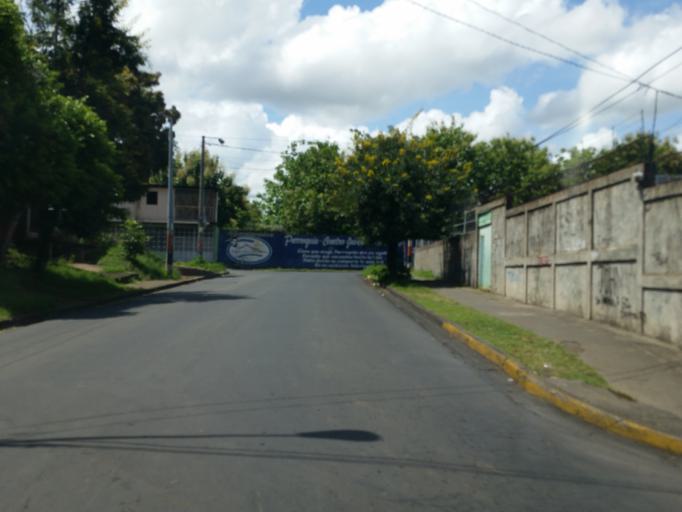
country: NI
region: Managua
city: Managua
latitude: 12.1320
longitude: -86.2397
